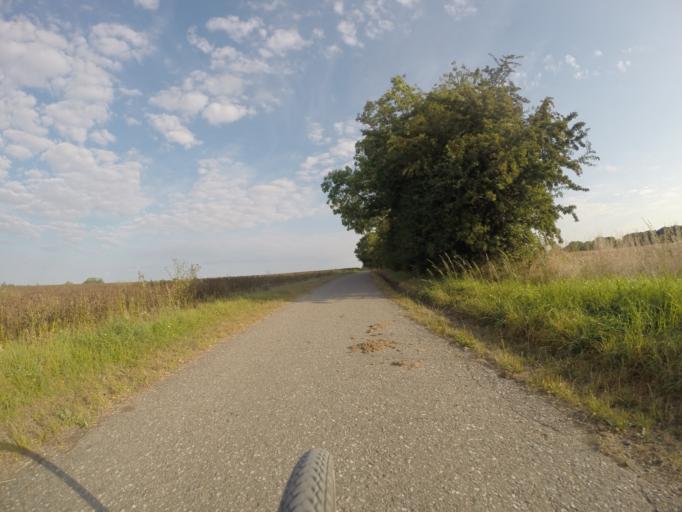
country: DK
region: Capital Region
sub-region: Egedal Kommune
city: Smorumnedre
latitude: 55.6963
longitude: 12.3146
